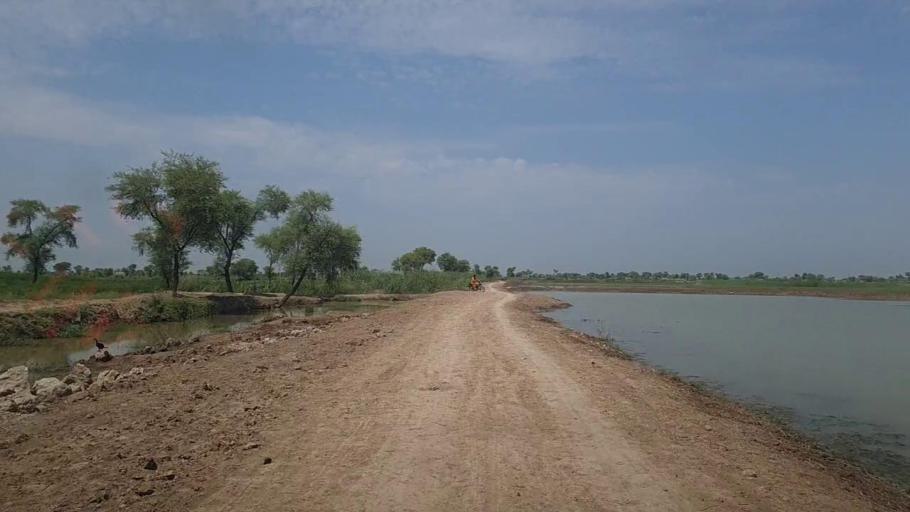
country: PK
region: Sindh
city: Thul
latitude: 28.3029
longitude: 68.6752
